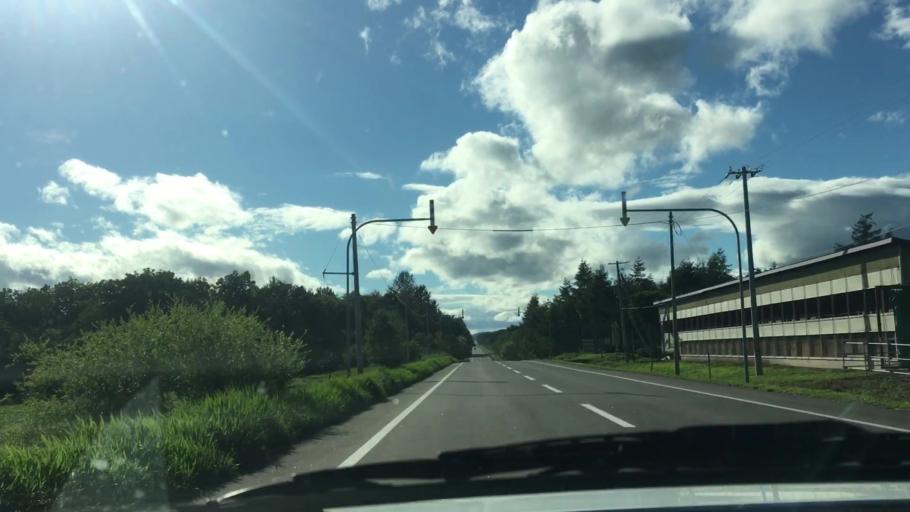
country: JP
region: Hokkaido
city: Otofuke
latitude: 43.1658
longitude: 143.1354
